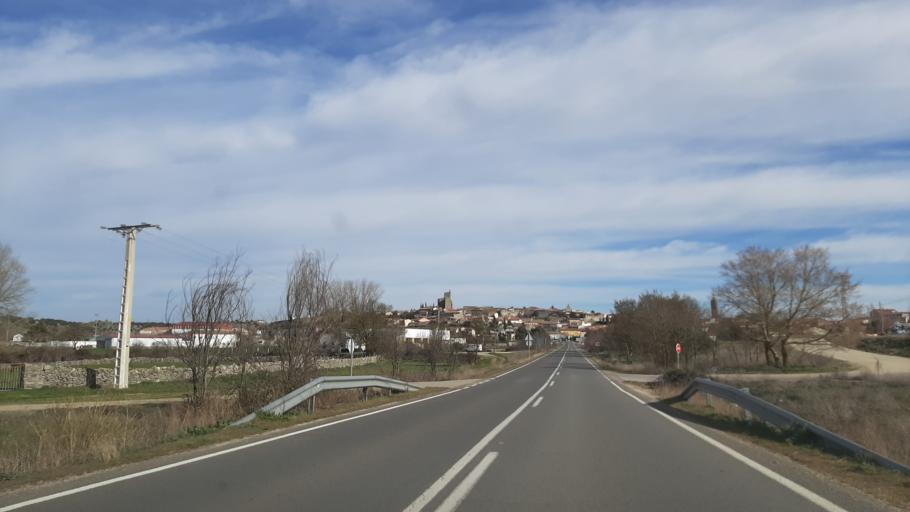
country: ES
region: Castille and Leon
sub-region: Provincia de Salamanca
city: Ledesma
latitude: 41.0908
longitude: -6.0110
